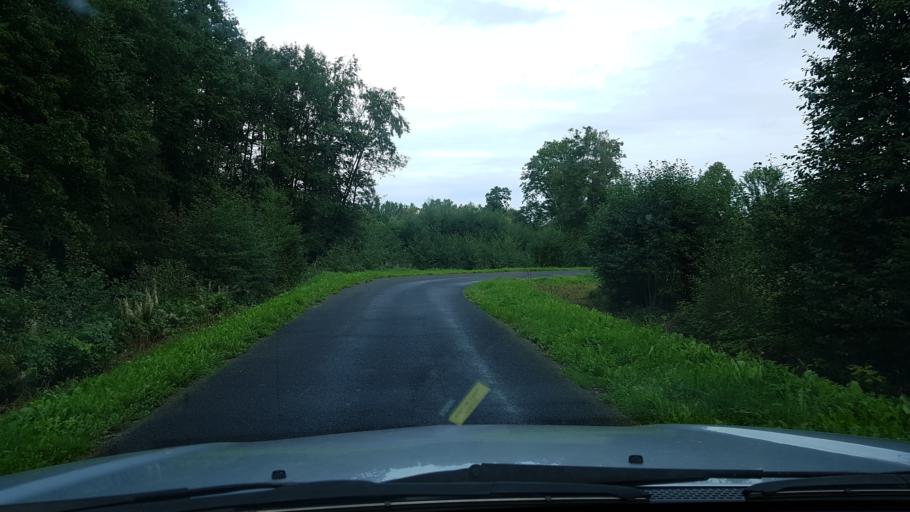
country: EE
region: Harju
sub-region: Rae vald
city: Jueri
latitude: 59.3574
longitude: 24.9360
